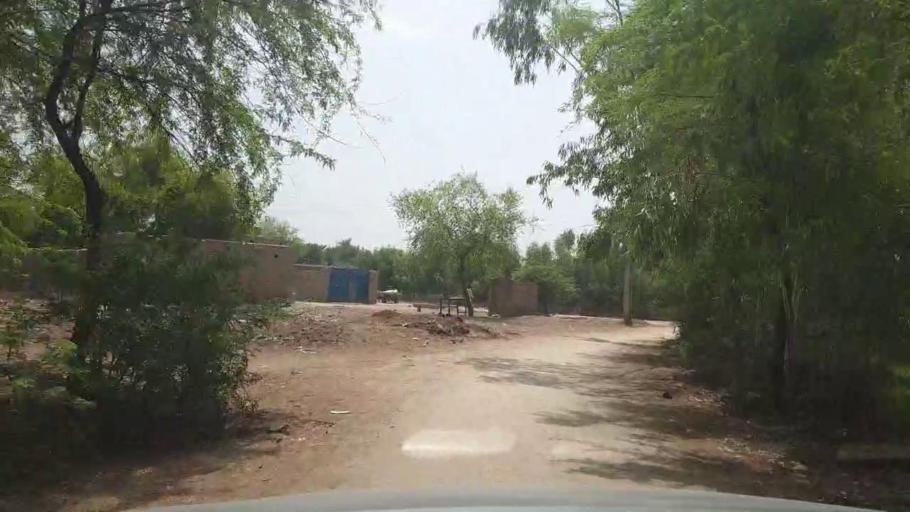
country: PK
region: Sindh
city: Garhi Yasin
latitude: 27.9275
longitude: 68.4017
